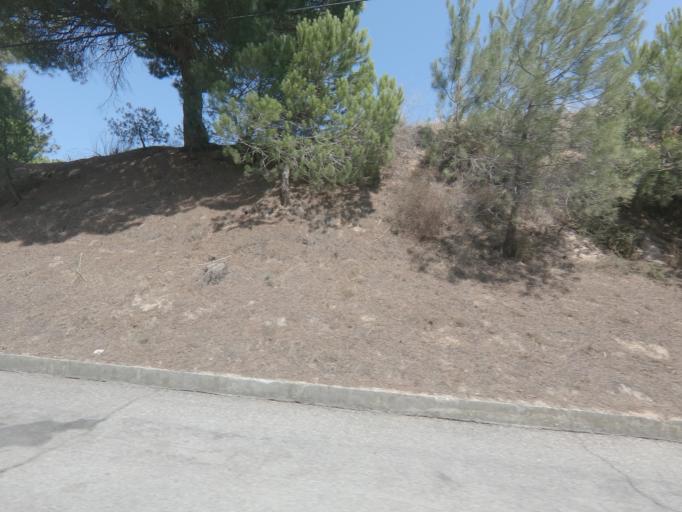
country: PT
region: Setubal
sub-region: Palmela
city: Palmela
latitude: 38.5583
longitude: -8.8870
